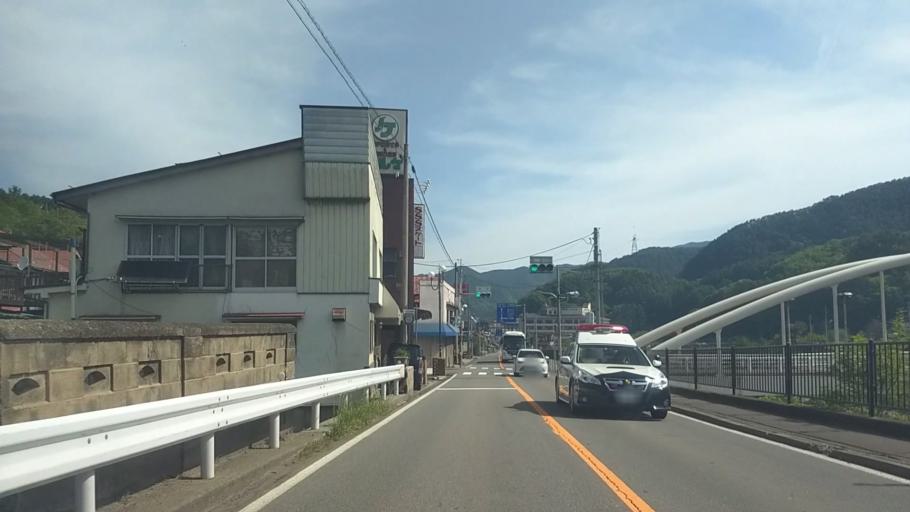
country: JP
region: Nagano
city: Saku
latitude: 36.0902
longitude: 138.4817
